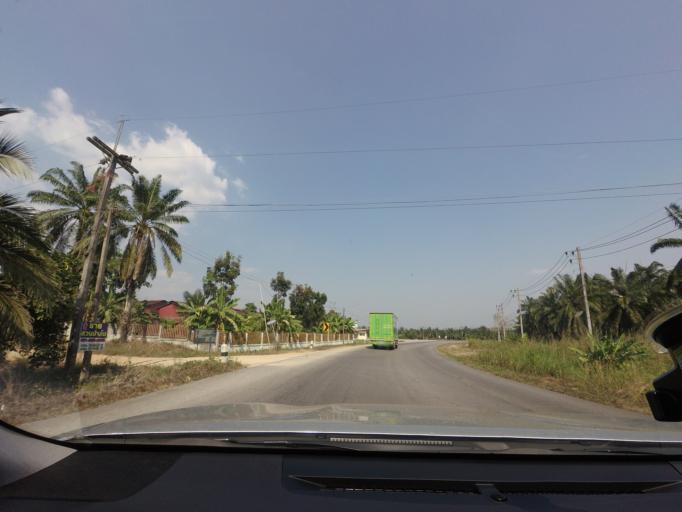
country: TH
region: Krabi
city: Plai Phraya
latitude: 8.5575
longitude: 98.7944
